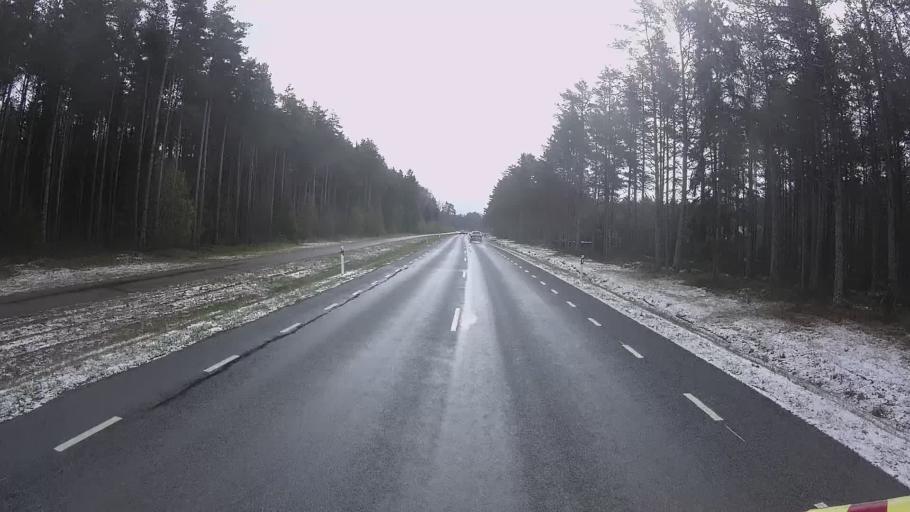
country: EE
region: Hiiumaa
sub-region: Kaerdla linn
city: Kardla
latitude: 58.9969
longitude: 22.7114
